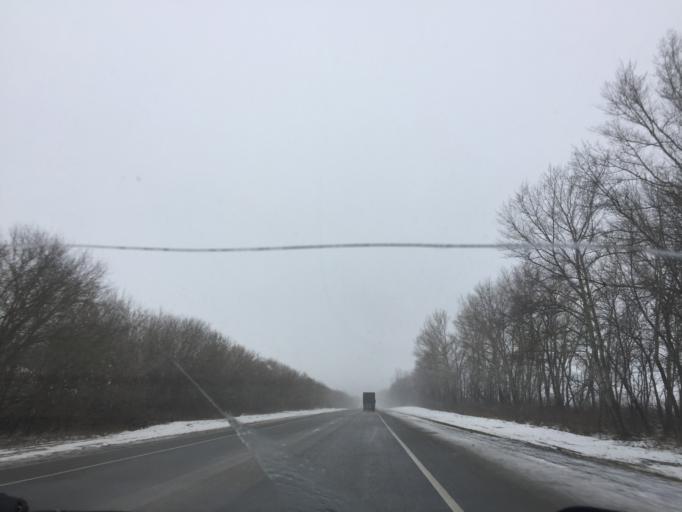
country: RU
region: Tula
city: Plavsk
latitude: 53.7703
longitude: 37.3481
